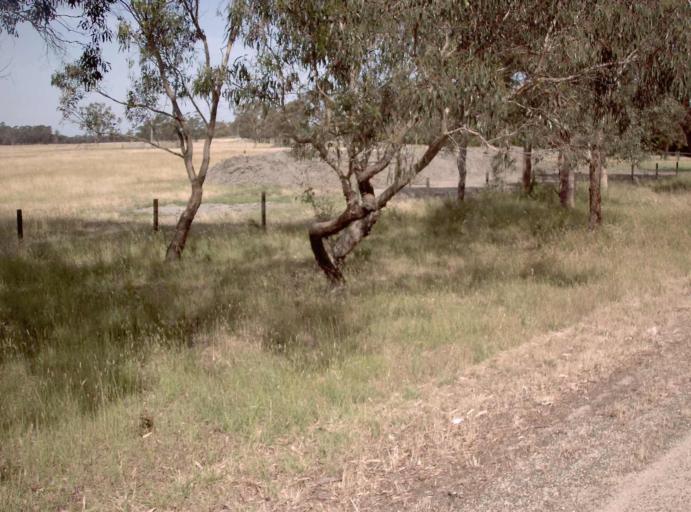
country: AU
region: Victoria
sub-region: Wellington
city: Sale
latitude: -38.2513
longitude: 147.1337
